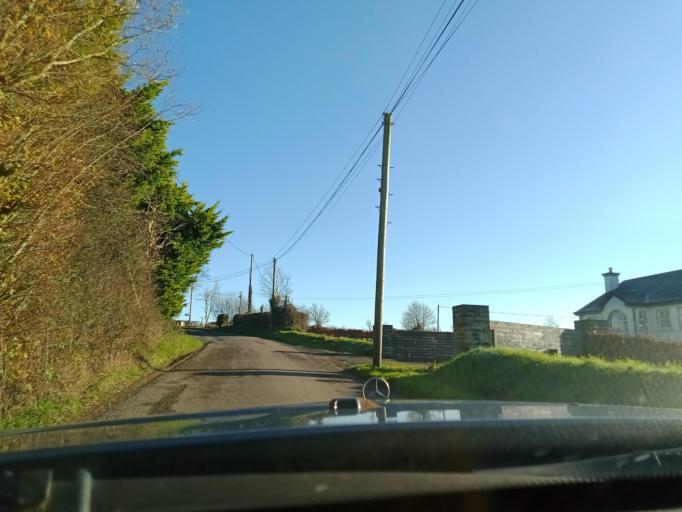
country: IE
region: Leinster
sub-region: Kilkenny
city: Mooncoin
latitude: 52.2996
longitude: -7.2210
